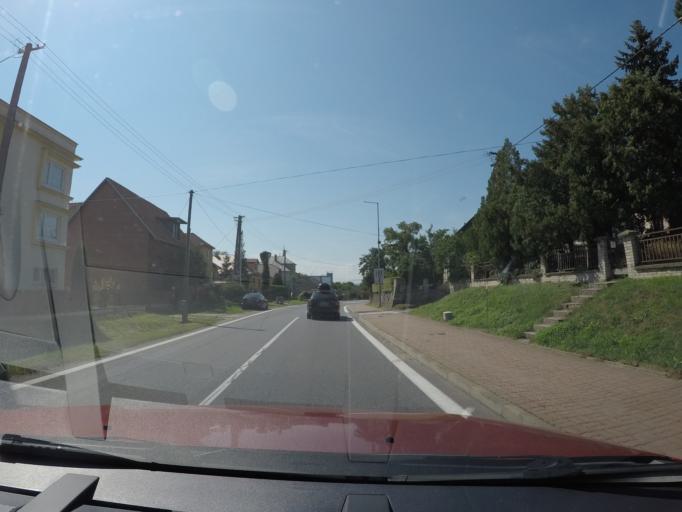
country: SK
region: Presovsky
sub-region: Okres Presov
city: Presov
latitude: 48.9267
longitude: 21.2413
